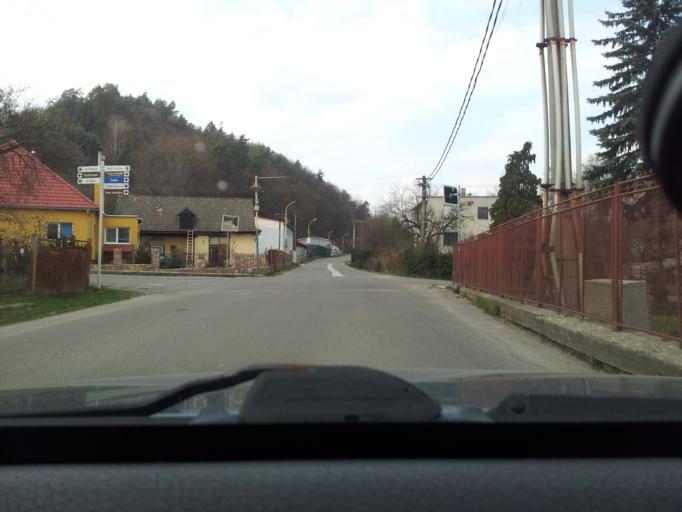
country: SK
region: Banskobystricky
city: Nova Bana
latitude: 48.4301
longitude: 18.6360
